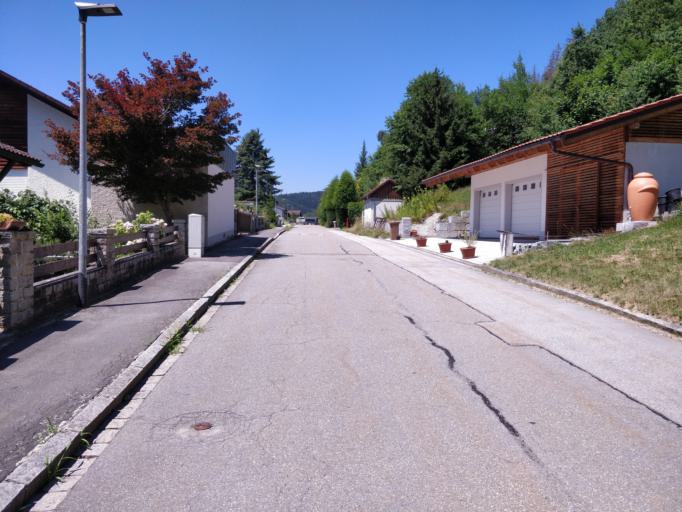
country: DE
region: Bavaria
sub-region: Lower Bavaria
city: Obernzell
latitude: 48.5556
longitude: 13.6523
